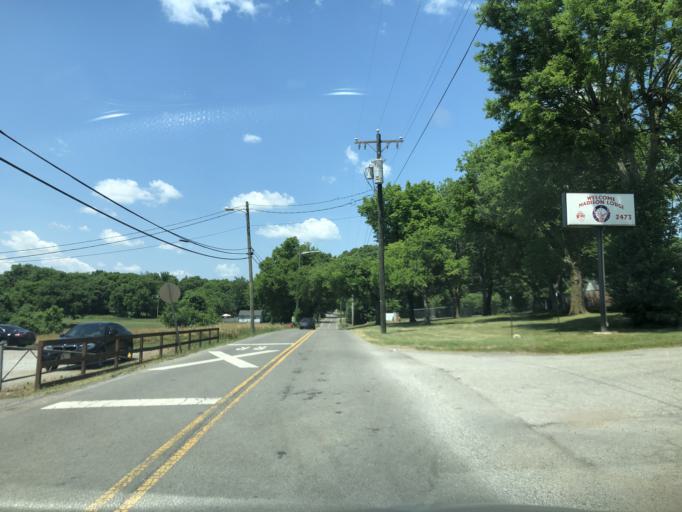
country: US
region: Tennessee
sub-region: Davidson County
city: Goodlettsville
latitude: 36.2676
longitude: -86.7145
